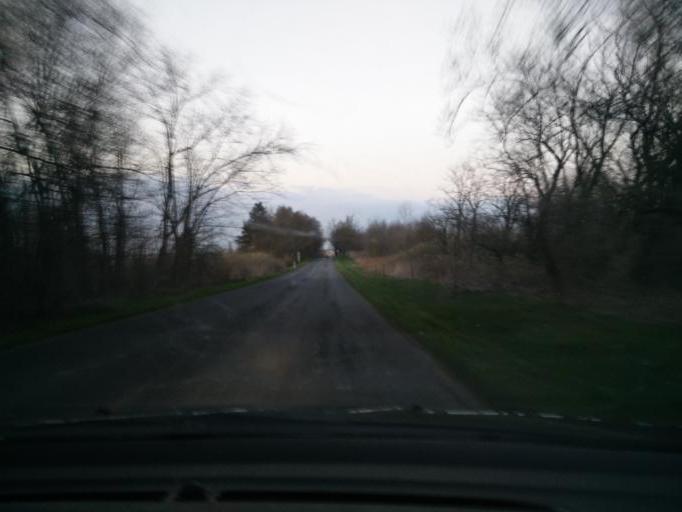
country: HU
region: Veszprem
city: Devecser
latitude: 47.0884
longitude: 17.4131
